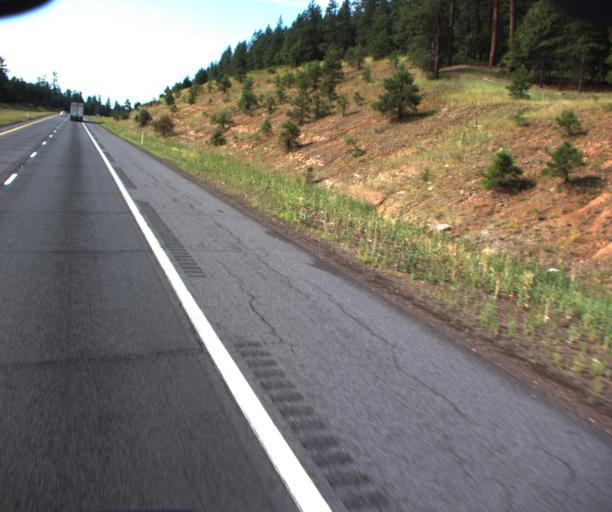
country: US
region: Arizona
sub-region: Coconino County
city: Mountainaire
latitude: 35.0382
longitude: -111.6850
